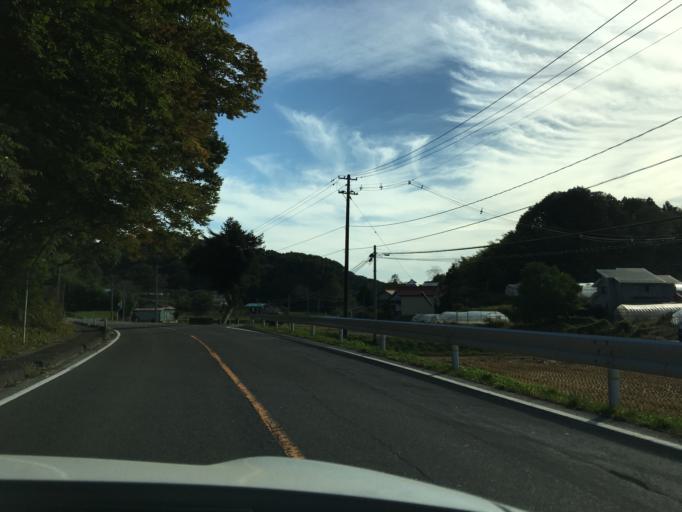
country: JP
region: Fukushima
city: Miharu
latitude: 37.4181
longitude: 140.4613
